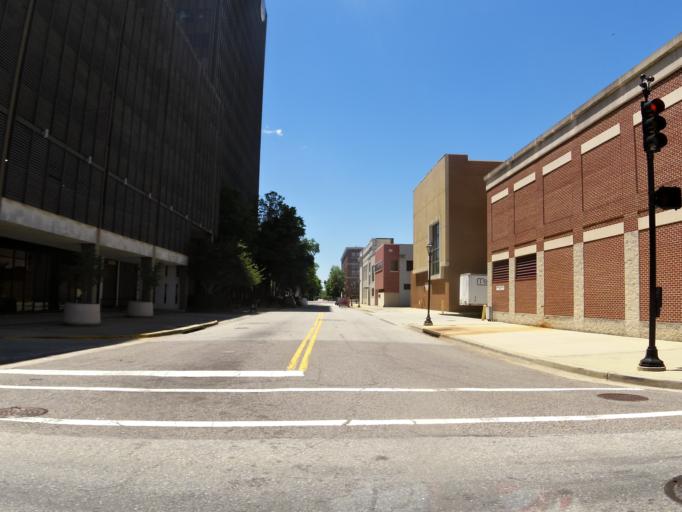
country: US
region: Georgia
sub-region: Richmond County
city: Augusta
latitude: 33.4759
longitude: -81.9627
